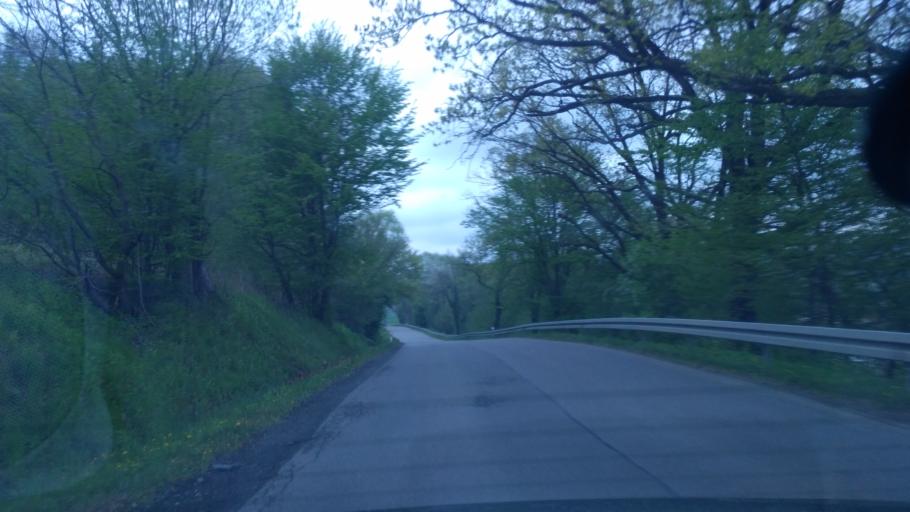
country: PL
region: Subcarpathian Voivodeship
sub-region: Powiat brzozowski
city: Nozdrzec
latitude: 49.7454
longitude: 22.2145
